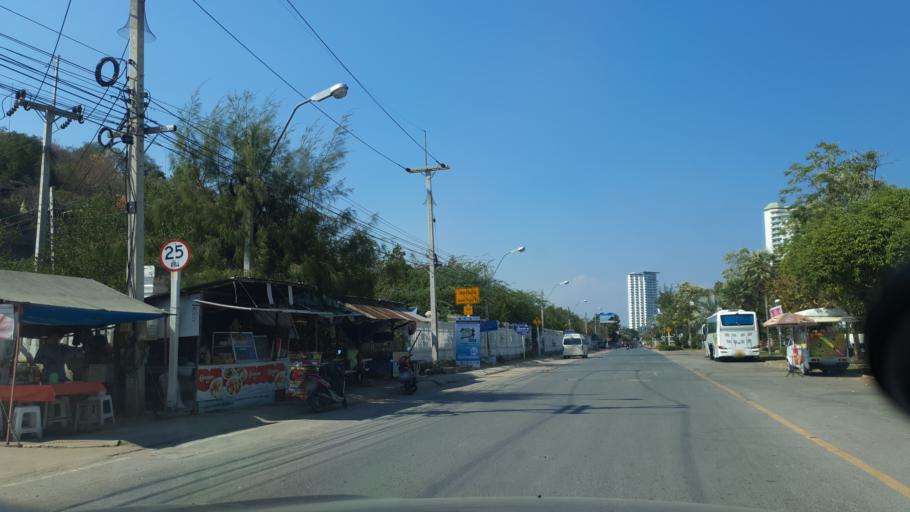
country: TH
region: Prachuap Khiri Khan
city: Hua Hin
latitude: 12.5190
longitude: 99.9760
